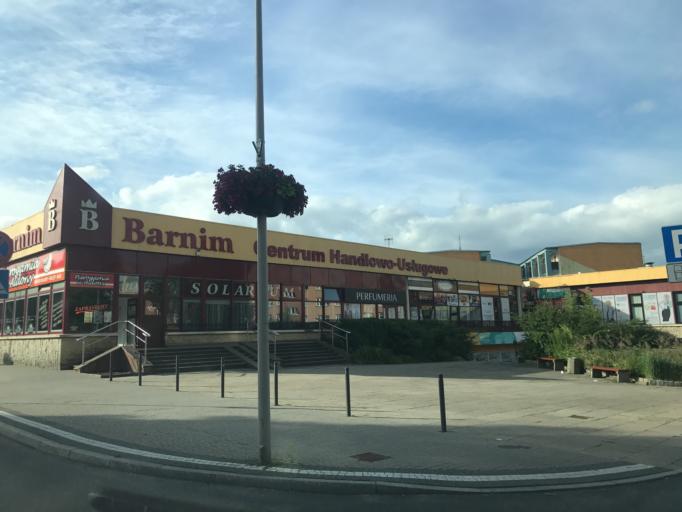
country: PL
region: West Pomeranian Voivodeship
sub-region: Powiat goleniowski
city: Goleniow
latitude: 53.5637
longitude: 14.8285
